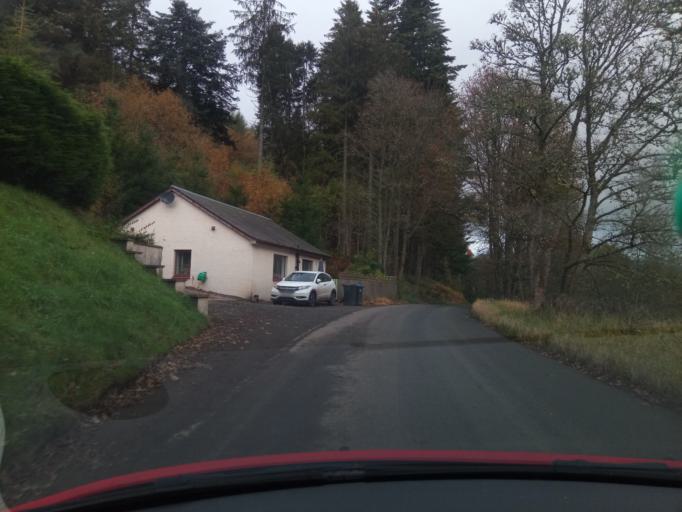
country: GB
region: Scotland
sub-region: The Scottish Borders
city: Innerleithen
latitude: 55.6213
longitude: -3.0930
